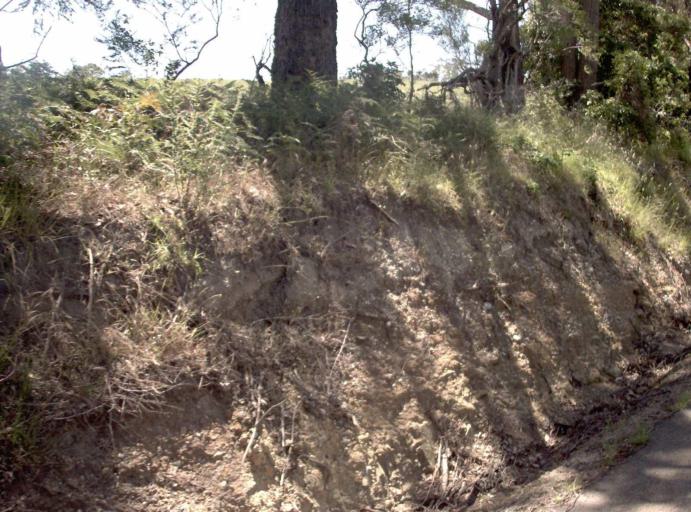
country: AU
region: Victoria
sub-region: East Gippsland
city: Lakes Entrance
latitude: -37.7050
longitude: 148.5536
